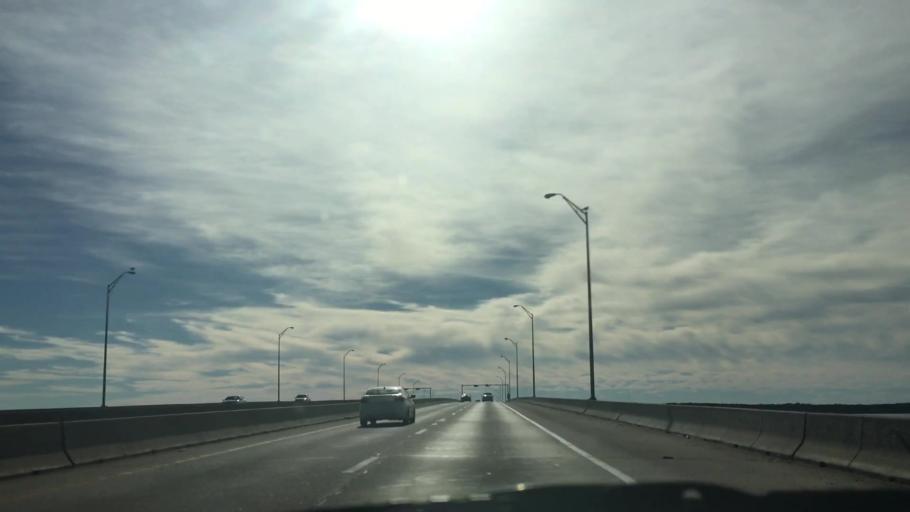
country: US
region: Virginia
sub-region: City of Newport News
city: Newport News
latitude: 36.9202
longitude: -76.4102
